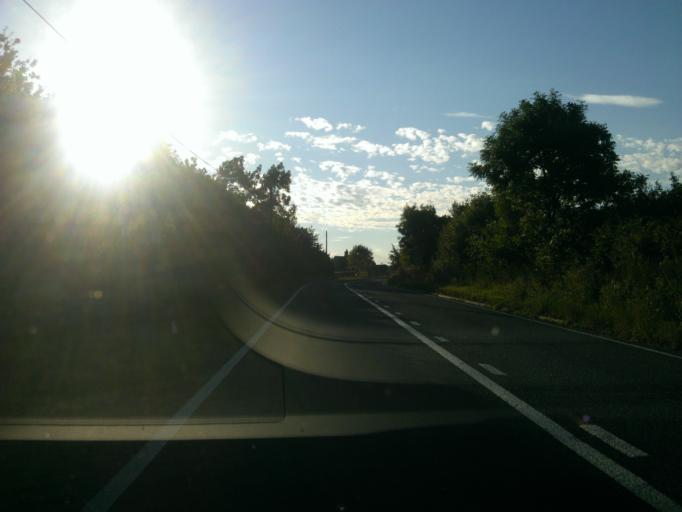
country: GB
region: England
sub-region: Essex
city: Alresford
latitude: 51.8687
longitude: 0.9834
